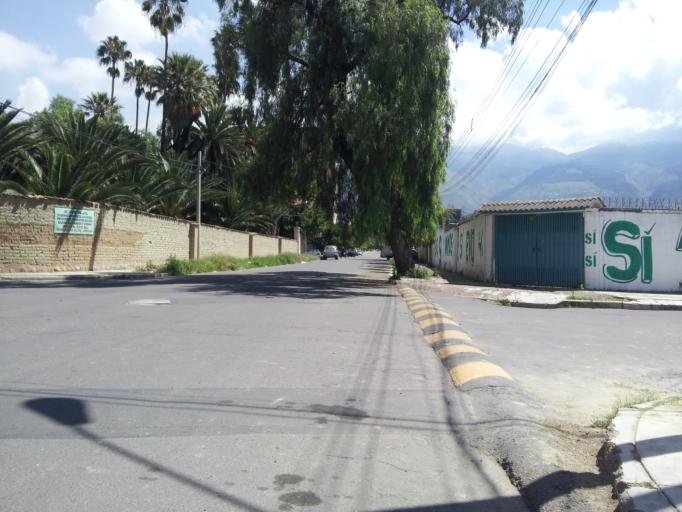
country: BO
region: Cochabamba
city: Cochabamba
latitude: -17.3775
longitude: -66.1711
